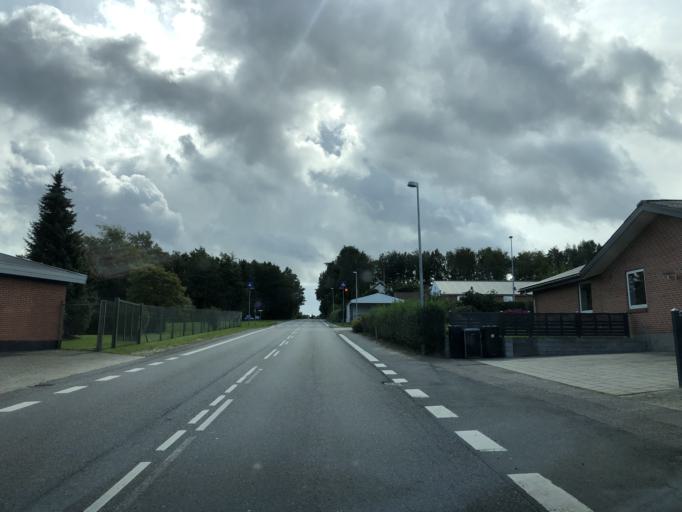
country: DK
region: Central Jutland
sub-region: Favrskov Kommune
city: Hadsten
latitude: 56.3210
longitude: 10.0358
